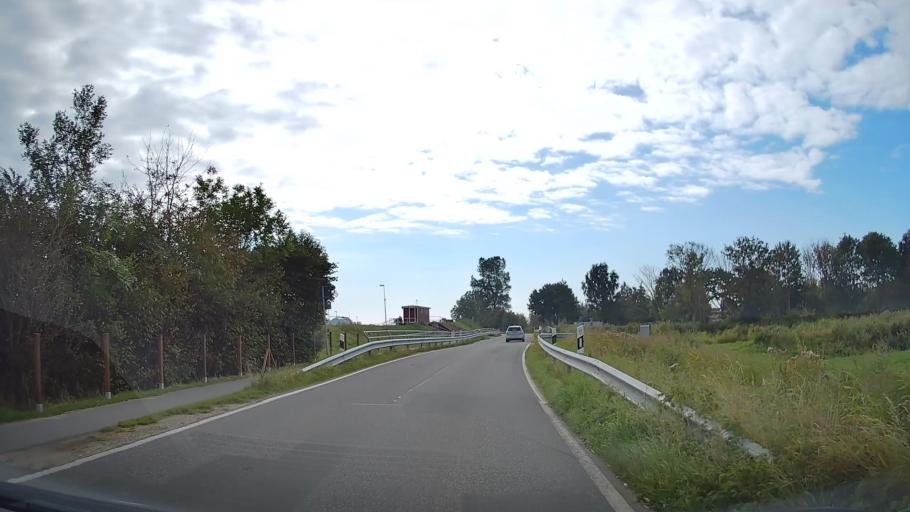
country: DE
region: Schleswig-Holstein
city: Blekendorf
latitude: 54.3367
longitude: 10.6451
